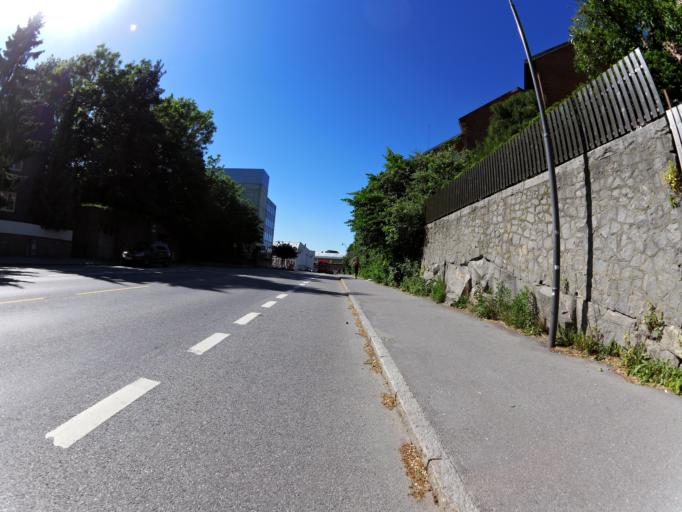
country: NO
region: Ostfold
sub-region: Fredrikstad
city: Fredrikstad
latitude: 59.2112
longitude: 10.9421
